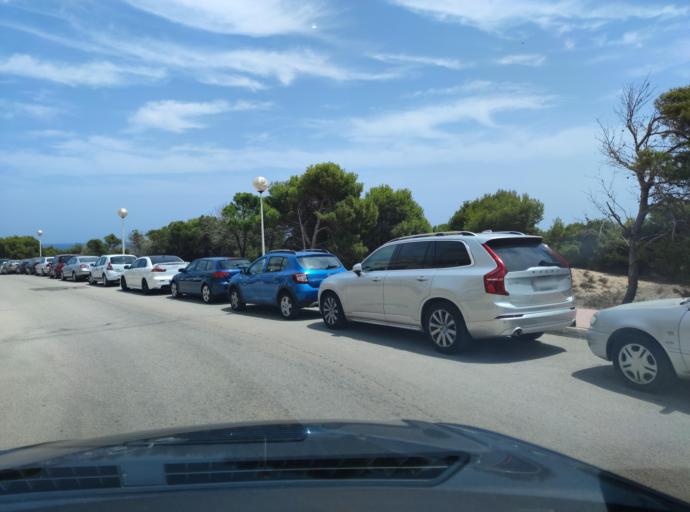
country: ES
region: Valencia
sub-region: Provincia de Alicante
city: Guardamar del Segura
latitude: 38.0620
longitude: -0.6543
